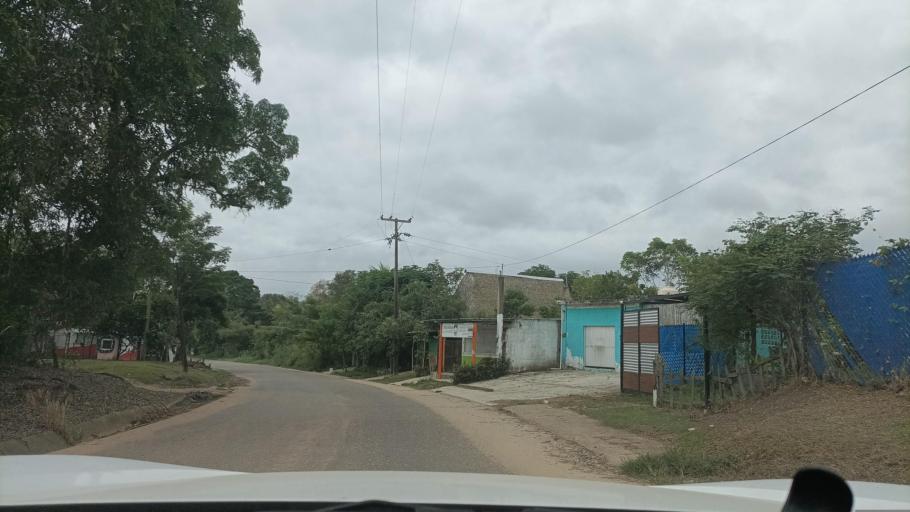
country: MX
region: Veracruz
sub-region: Cosoleacaque
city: Coacotla
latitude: 17.9516
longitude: -94.7196
